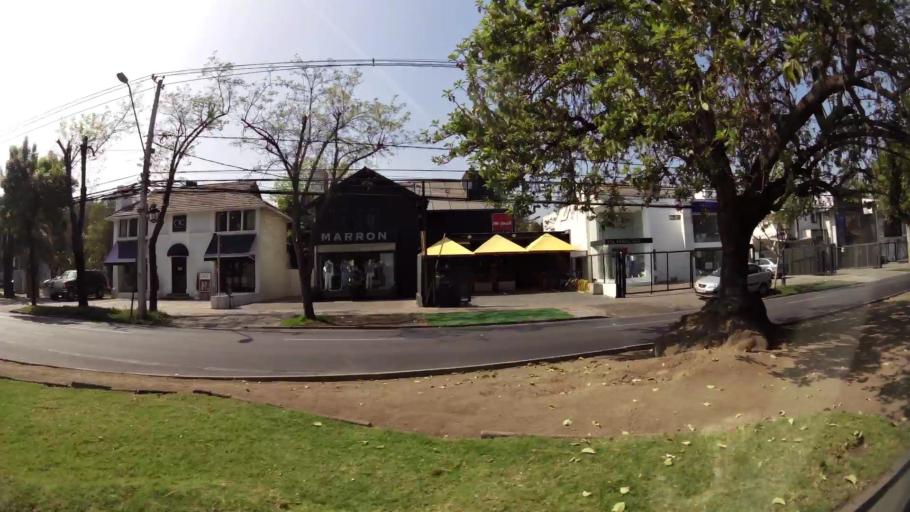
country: CL
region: Santiago Metropolitan
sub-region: Provincia de Santiago
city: Villa Presidente Frei, Nunoa, Santiago, Chile
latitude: -33.3994
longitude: -70.5980
